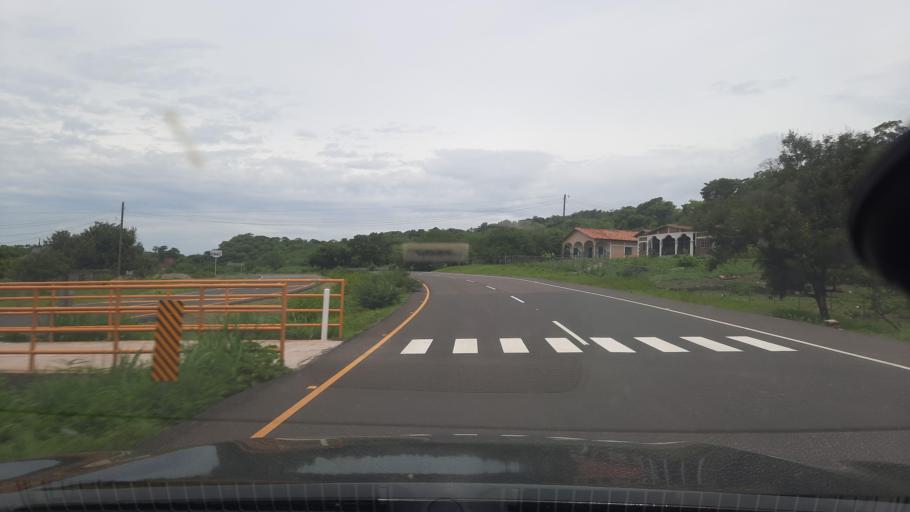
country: HN
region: Valle
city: Aramecina
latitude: 13.7539
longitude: -87.7158
